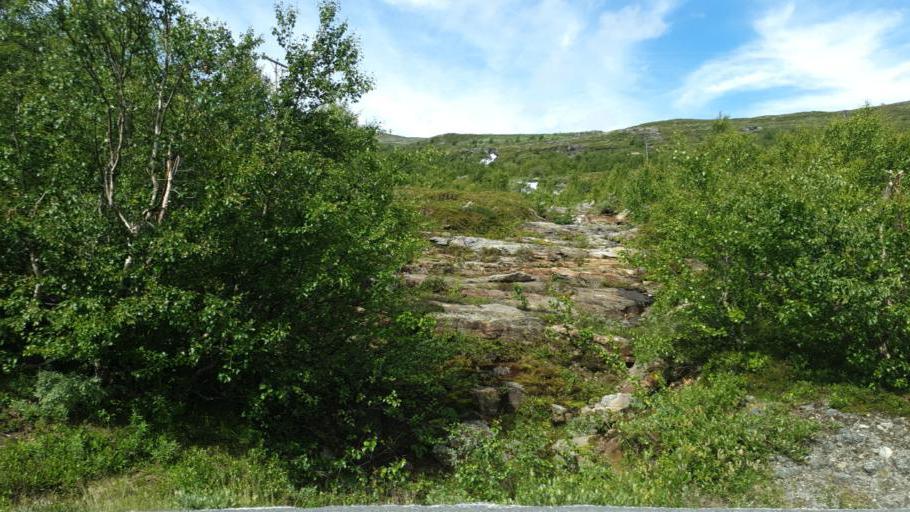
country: NO
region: Oppland
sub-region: Lom
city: Fossbergom
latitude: 61.5115
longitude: 8.8443
